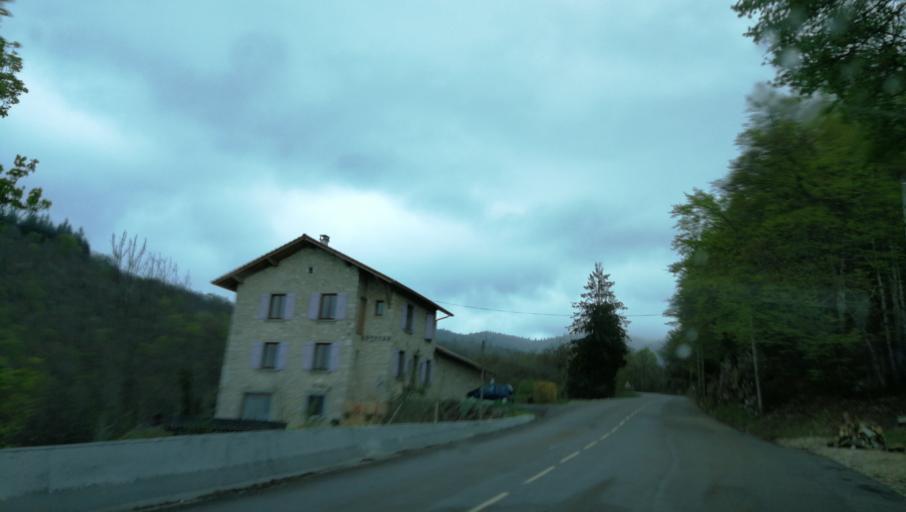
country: FR
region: Rhone-Alpes
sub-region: Departement de la Drome
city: Saint-Laurent-en-Royans
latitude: 45.0087
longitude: 5.3189
